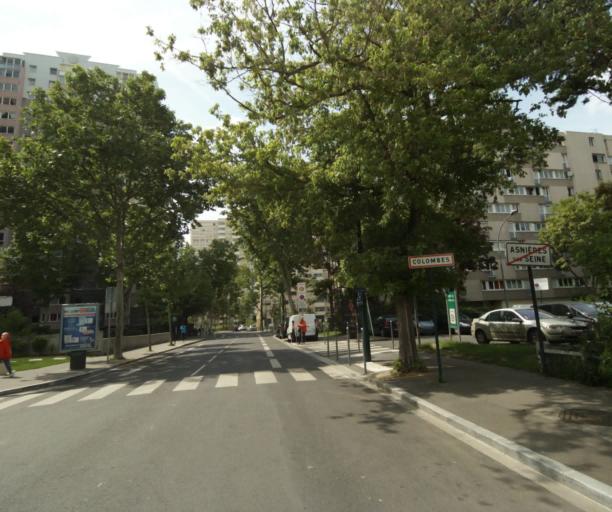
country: FR
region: Ile-de-France
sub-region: Departement des Hauts-de-Seine
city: Bois-Colombes
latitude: 48.9323
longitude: 2.2729
